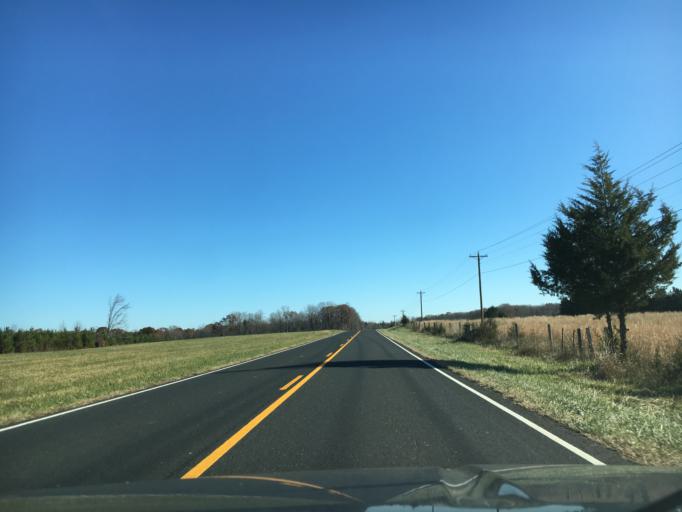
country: US
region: Virginia
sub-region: Appomattox County
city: Appomattox
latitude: 37.4252
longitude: -78.7363
